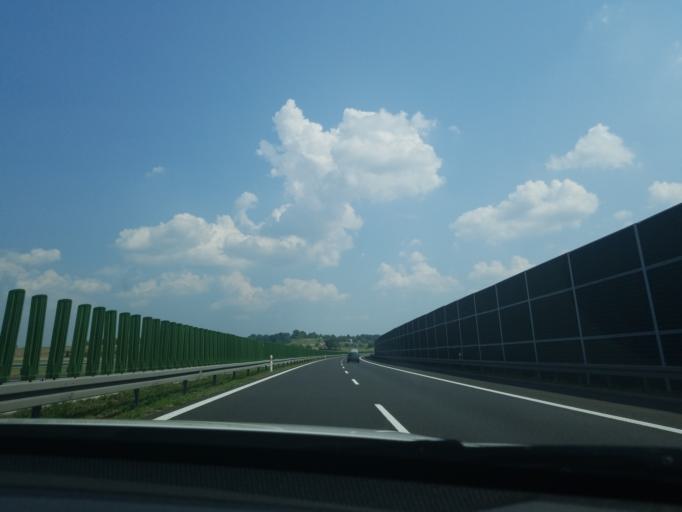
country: PL
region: Lesser Poland Voivodeship
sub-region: Powiat tarnowski
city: Lukowa
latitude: 50.0643
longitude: 20.9652
